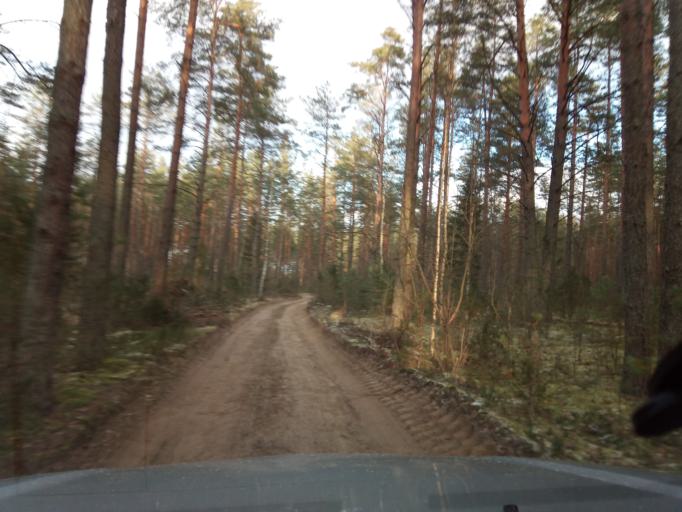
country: LT
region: Alytaus apskritis
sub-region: Alytaus rajonas
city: Daugai
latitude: 54.1090
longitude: 24.3014
